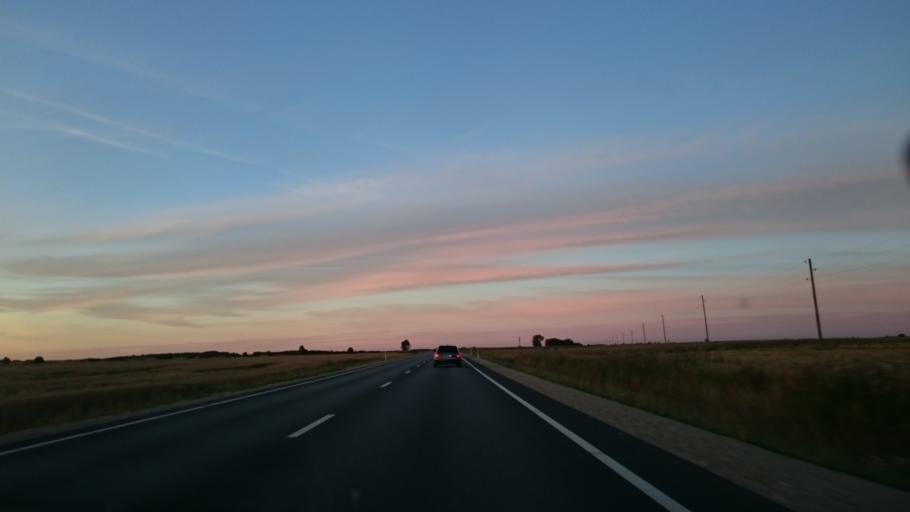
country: LV
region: Dobeles Rajons
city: Dobele
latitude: 56.7294
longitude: 23.2122
